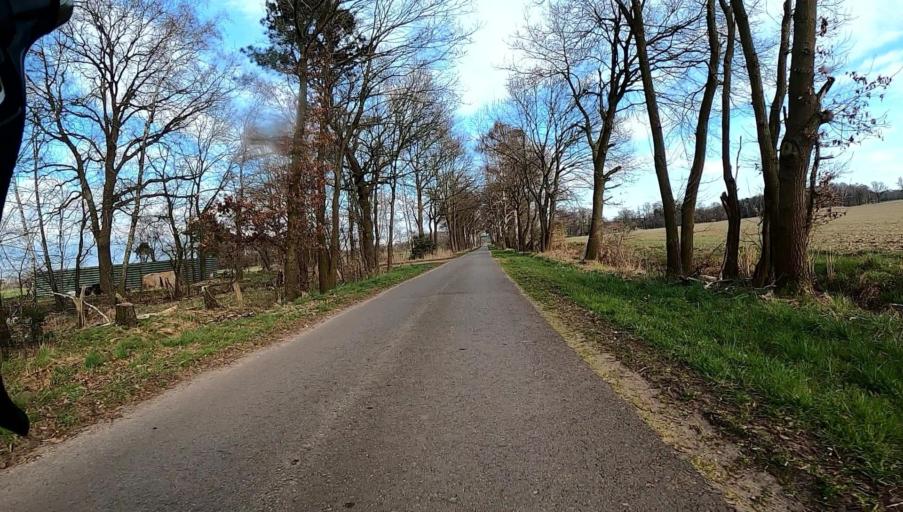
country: DE
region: Lower Saxony
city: Lindwedel
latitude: 52.5859
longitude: 9.6343
